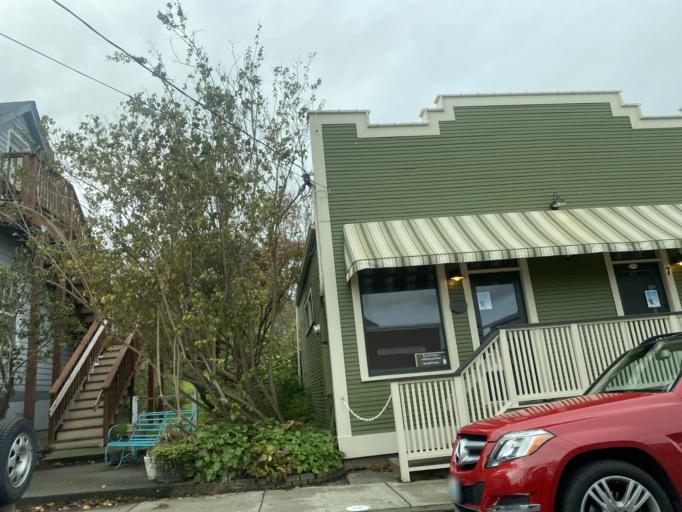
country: US
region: Washington
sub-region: Island County
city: Coupeville
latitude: 48.2211
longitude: -122.6867
